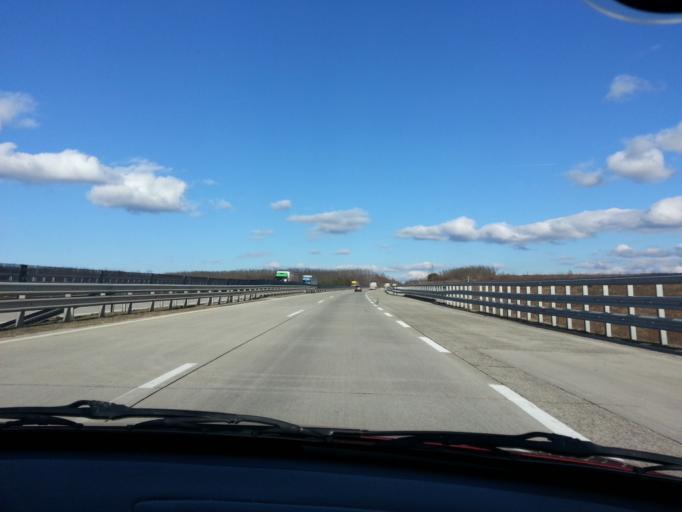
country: HU
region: Pest
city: Kerepes
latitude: 47.5580
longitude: 19.3170
